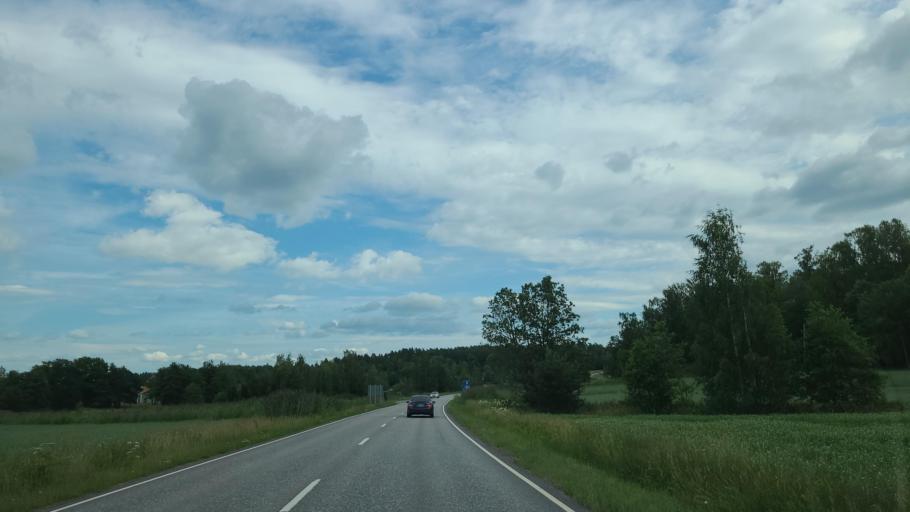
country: FI
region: Varsinais-Suomi
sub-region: Turku
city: Rymaettylae
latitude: 60.3807
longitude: 21.9411
